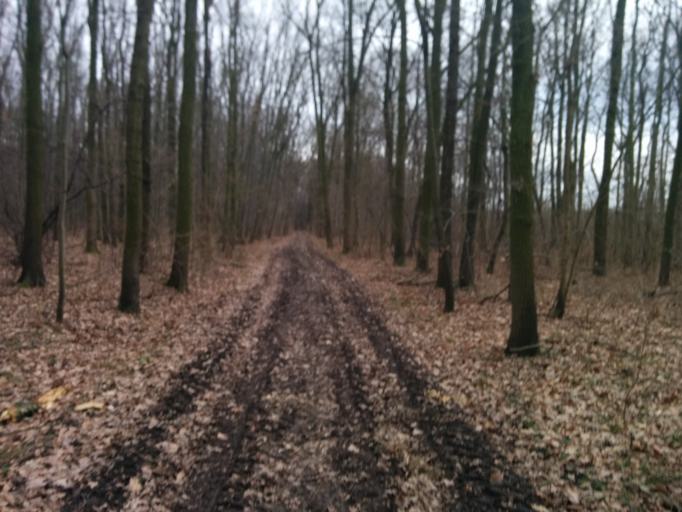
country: CZ
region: Central Bohemia
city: Libis
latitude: 50.2815
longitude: 14.5064
